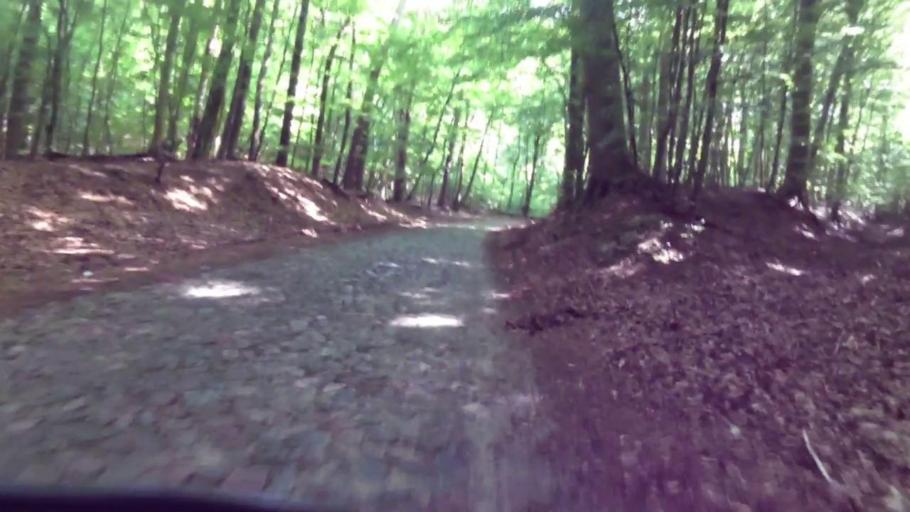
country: PL
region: West Pomeranian Voivodeship
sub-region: Powiat kamienski
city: Miedzyzdroje
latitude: 53.8783
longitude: 14.4670
